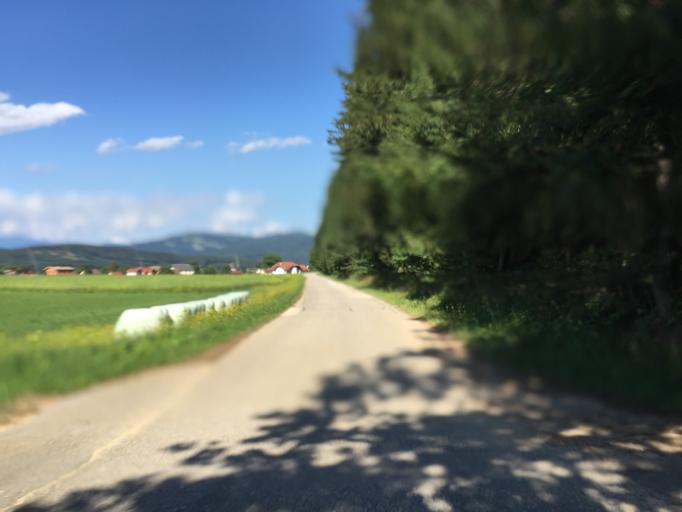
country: AT
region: Carinthia
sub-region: Politischer Bezirk Volkermarkt
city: Feistritz ob Bleiburg
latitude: 46.5631
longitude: 14.7510
